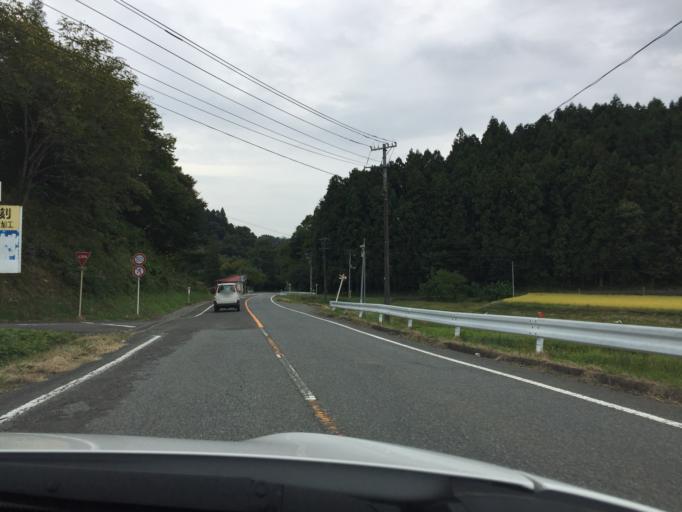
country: JP
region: Fukushima
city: Nihommatsu
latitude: 37.6052
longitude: 140.5354
